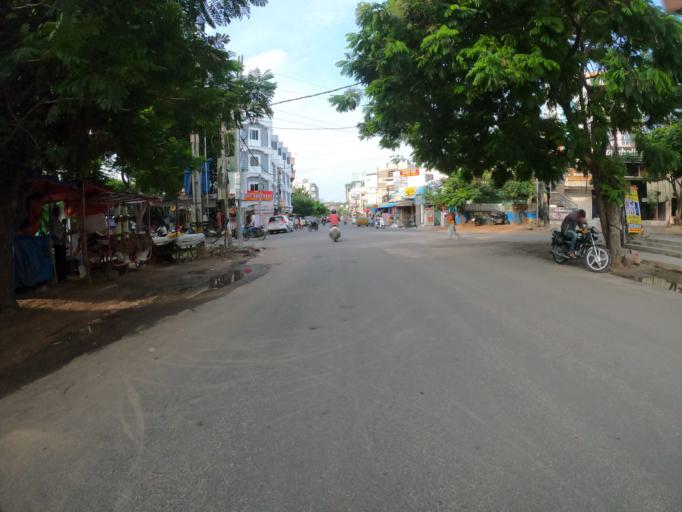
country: IN
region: Telangana
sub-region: Hyderabad
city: Hyderabad
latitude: 17.4068
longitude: 78.3919
